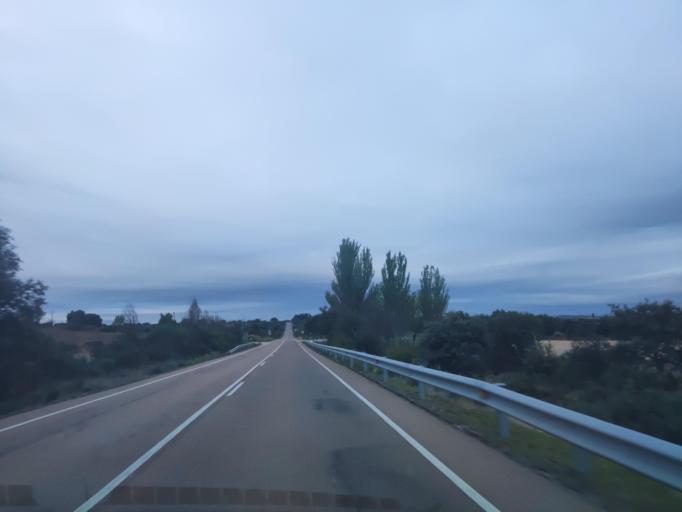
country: ES
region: Castille and Leon
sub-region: Provincia de Salamanca
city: Lumbrales
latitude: 40.9414
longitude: -6.7447
